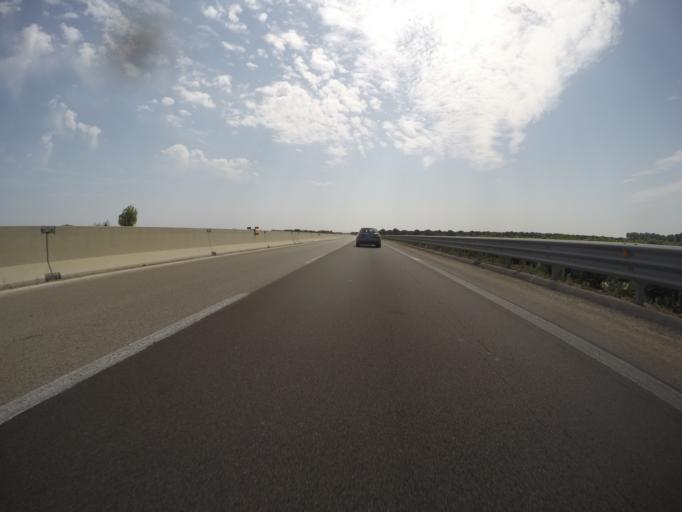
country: IT
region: Apulia
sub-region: Provincia di Brindisi
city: Latiano
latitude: 40.5642
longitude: 17.7505
